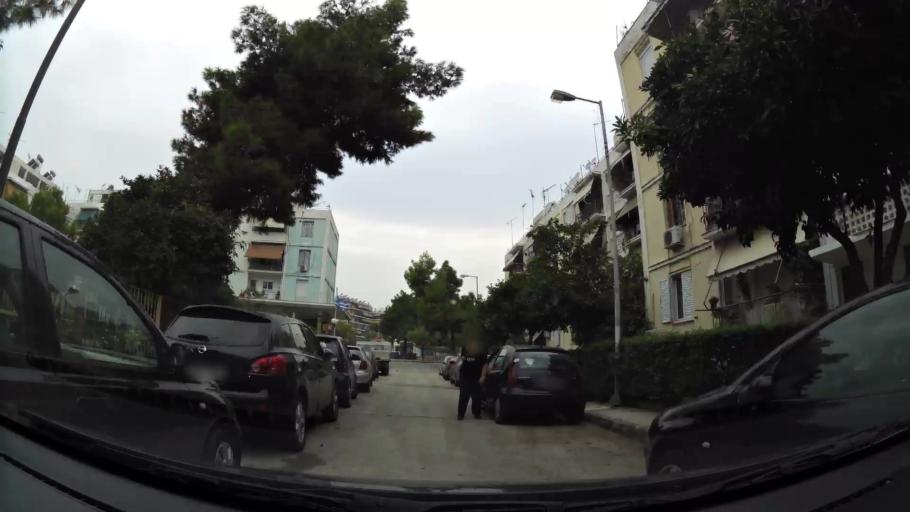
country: GR
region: Attica
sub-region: Nomos Piraios
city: Agios Ioannis Rentis
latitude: 37.9734
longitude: 23.6662
